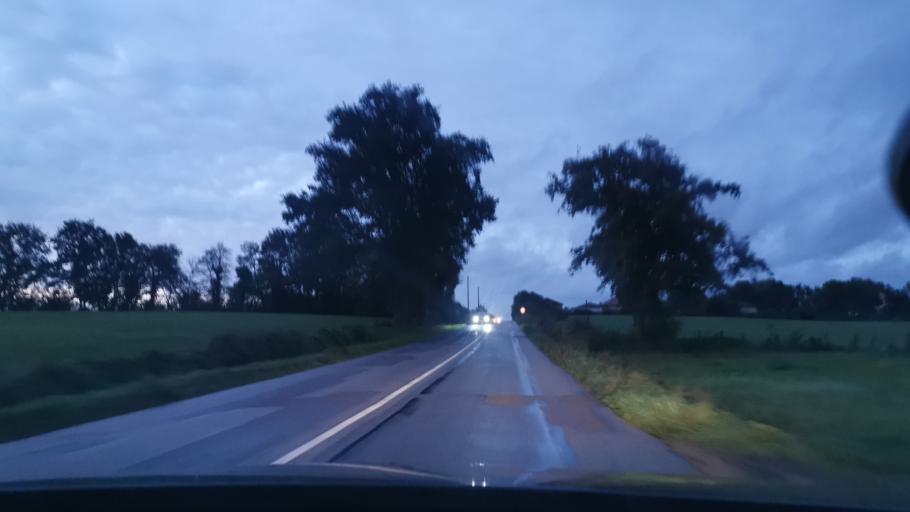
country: FR
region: Rhone-Alpes
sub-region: Departement de l'Ain
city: Bage-la-Ville
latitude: 46.3482
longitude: 4.9405
